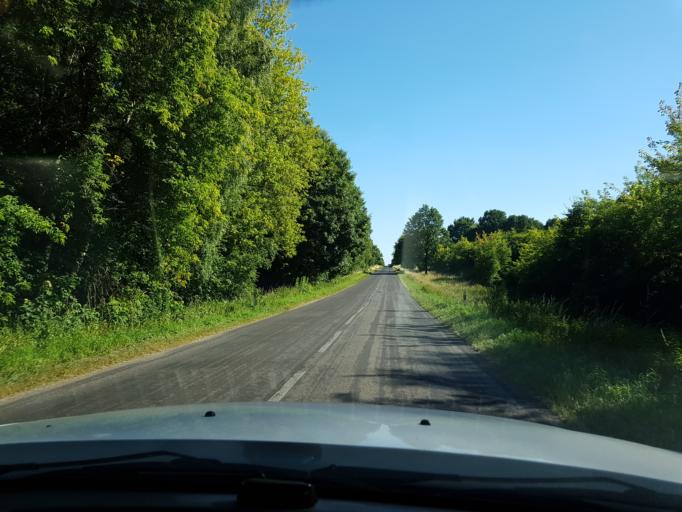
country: PL
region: West Pomeranian Voivodeship
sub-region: Powiat lobeski
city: Lobez
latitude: 53.6851
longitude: 15.6069
